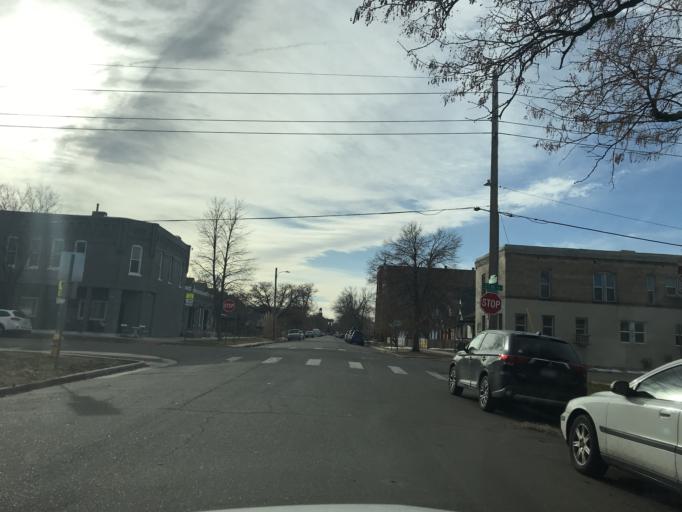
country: US
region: Colorado
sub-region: Denver County
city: Denver
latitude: 39.7686
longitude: -104.9696
